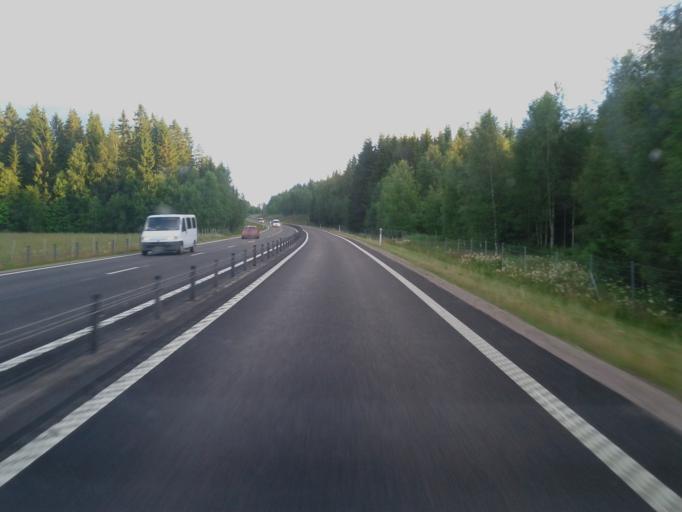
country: SE
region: Dalarna
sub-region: Borlange Kommun
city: Borlaenge
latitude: 60.4547
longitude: 15.3717
